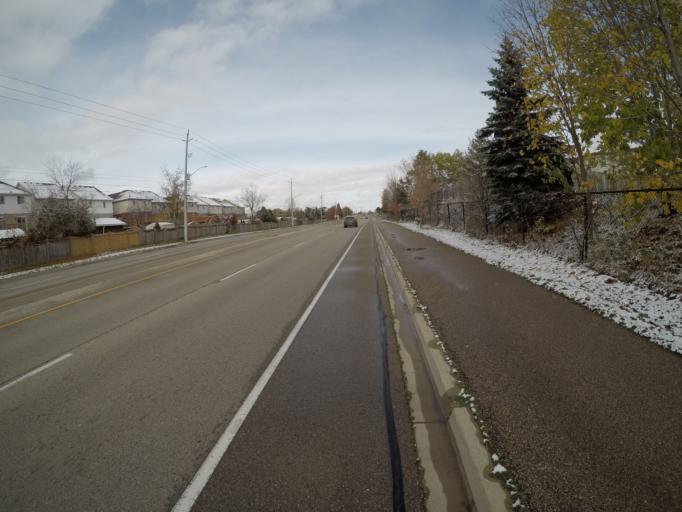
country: CA
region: Ontario
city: Waterloo
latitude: 43.5070
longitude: -80.4974
